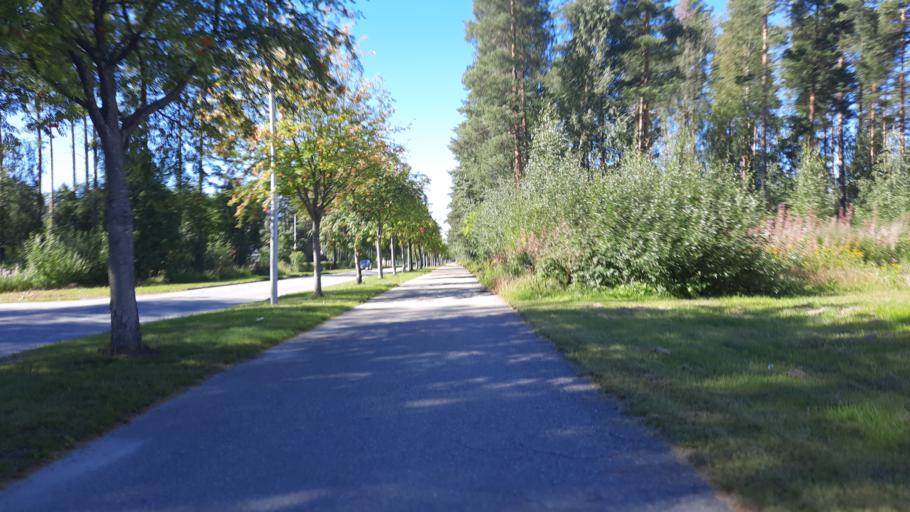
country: FI
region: North Karelia
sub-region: Joensuu
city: Joensuu
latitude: 62.6216
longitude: 29.7530
